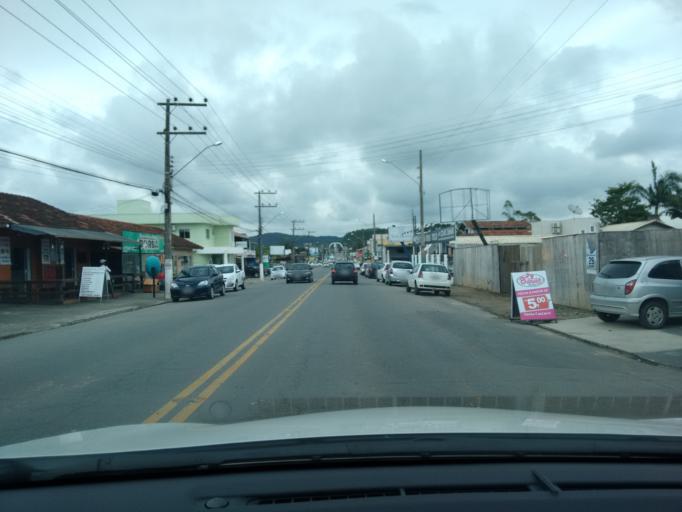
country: BR
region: Santa Catarina
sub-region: Penha
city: Penha
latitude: -26.7600
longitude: -48.6802
